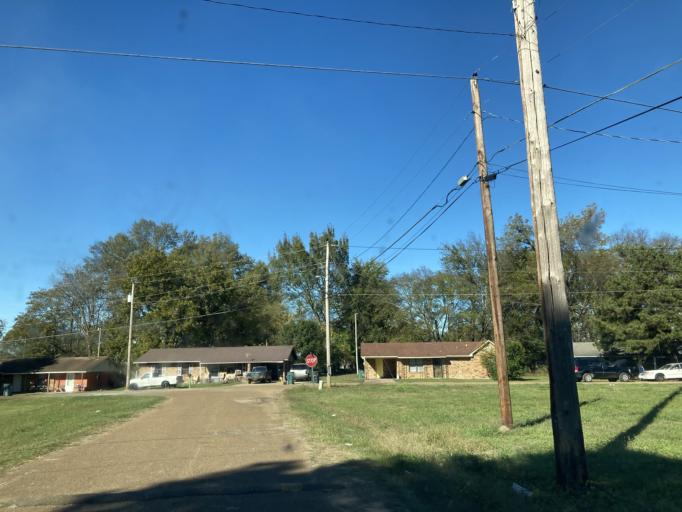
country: US
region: Mississippi
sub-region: Yazoo County
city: Yazoo City
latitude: 32.8430
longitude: -90.4231
